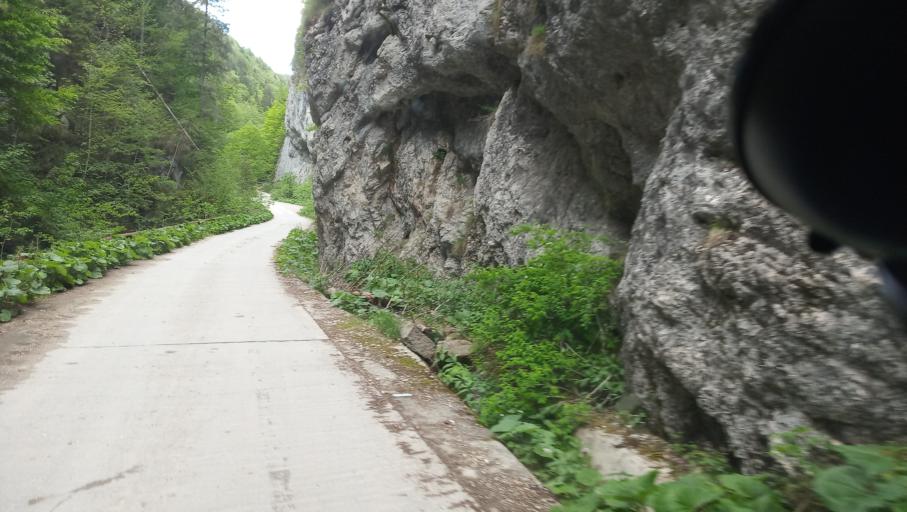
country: RO
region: Alba
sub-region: Comuna Scarisoara
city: Scarisoara
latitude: 46.4740
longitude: 22.8473
